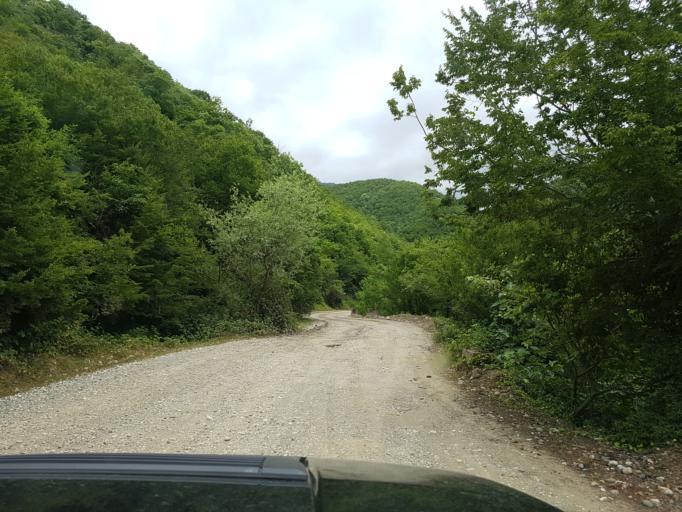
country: GE
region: Imereti
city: Kutaisi
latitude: 42.4371
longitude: 42.7467
